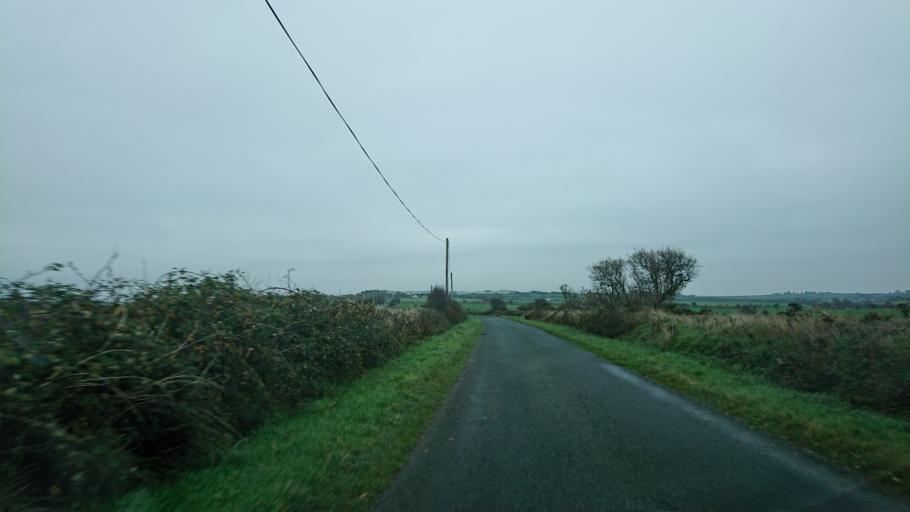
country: IE
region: Munster
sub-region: Waterford
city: Dunmore East
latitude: 52.1520
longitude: -7.0446
